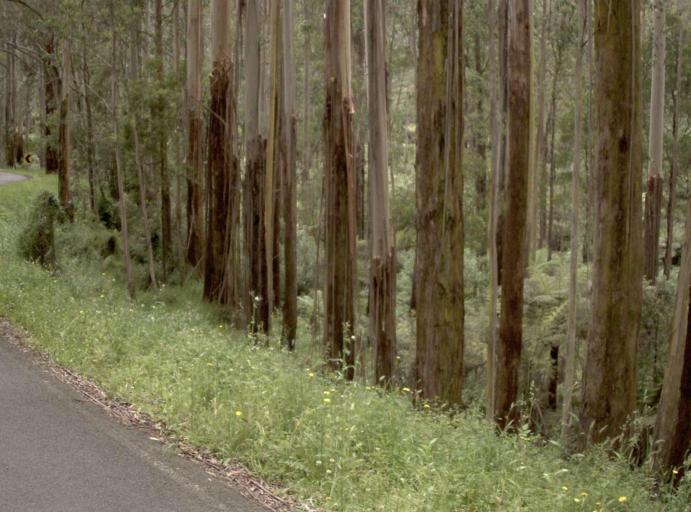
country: AU
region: Victoria
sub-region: Baw Baw
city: Warragul
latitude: -37.8912
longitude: 146.0957
